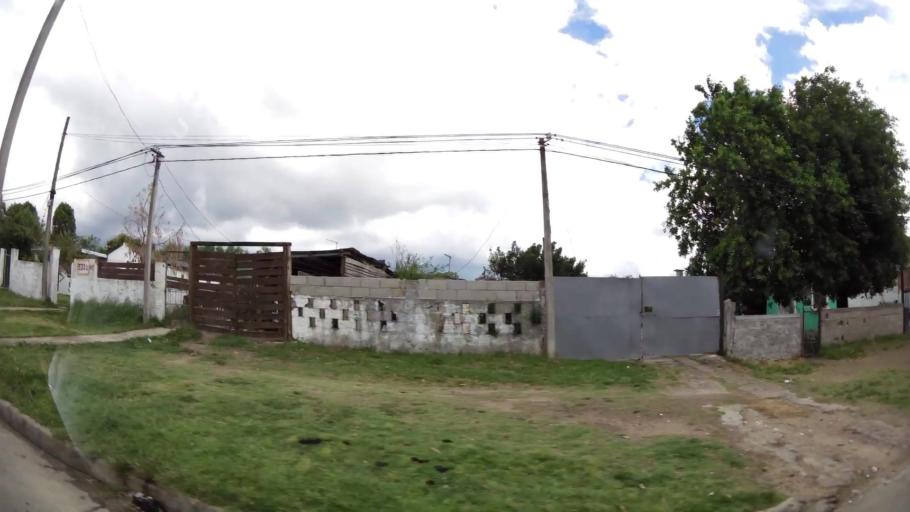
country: UY
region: Montevideo
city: Montevideo
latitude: -34.8255
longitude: -56.1656
